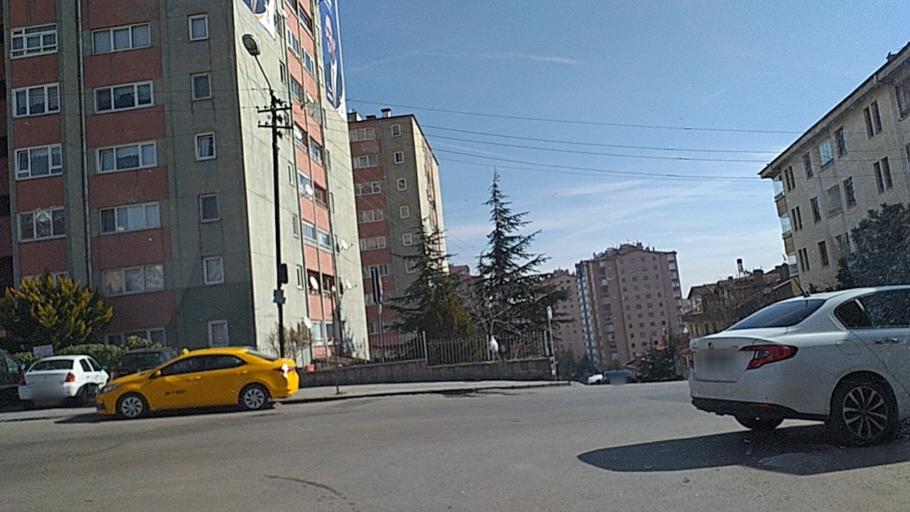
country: TR
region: Ankara
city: Ankara
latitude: 39.9819
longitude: 32.8354
